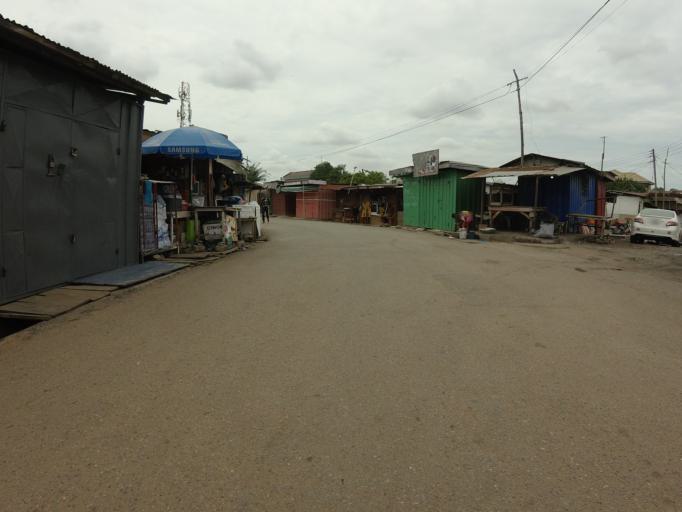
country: GH
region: Greater Accra
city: Accra
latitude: 5.5909
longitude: -0.2150
